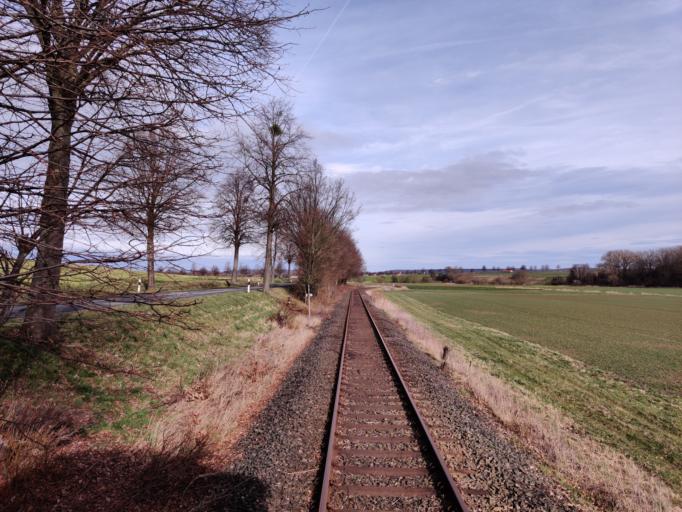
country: DE
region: Lower Saxony
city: Bockenem
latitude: 51.9913
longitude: 10.1191
